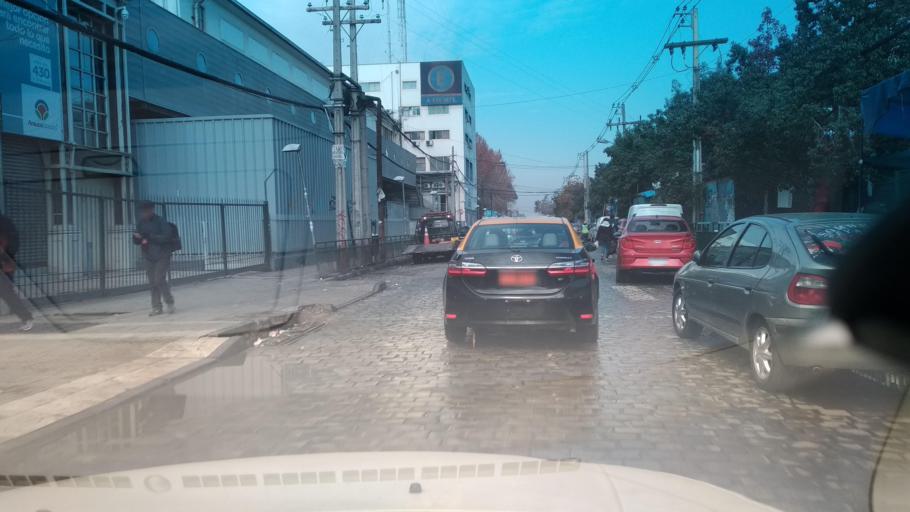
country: CL
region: Santiago Metropolitan
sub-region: Provincia de Santiago
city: Santiago
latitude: -33.4521
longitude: -70.6803
